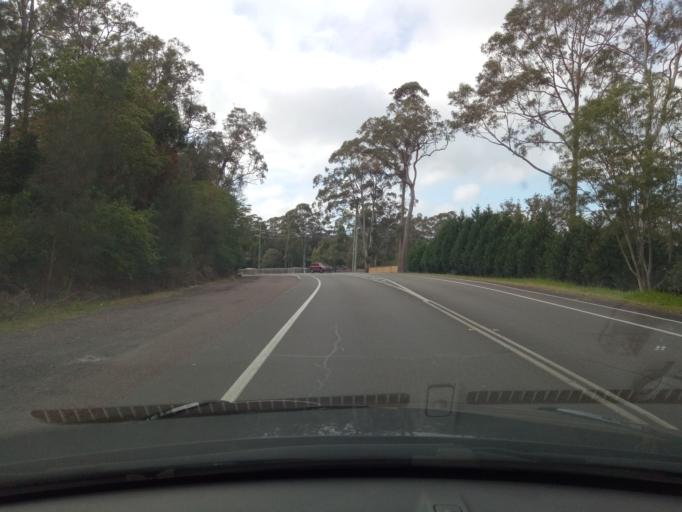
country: AU
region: New South Wales
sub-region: Gosford Shire
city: Erina
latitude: -33.4325
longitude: 151.3765
